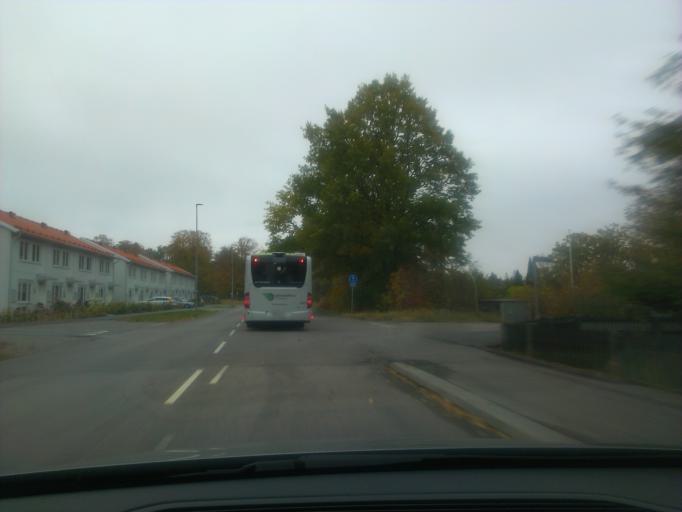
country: SE
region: Kronoberg
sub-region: Vaxjo Kommun
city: Vaexjoe
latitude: 56.9123
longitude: 14.7391
